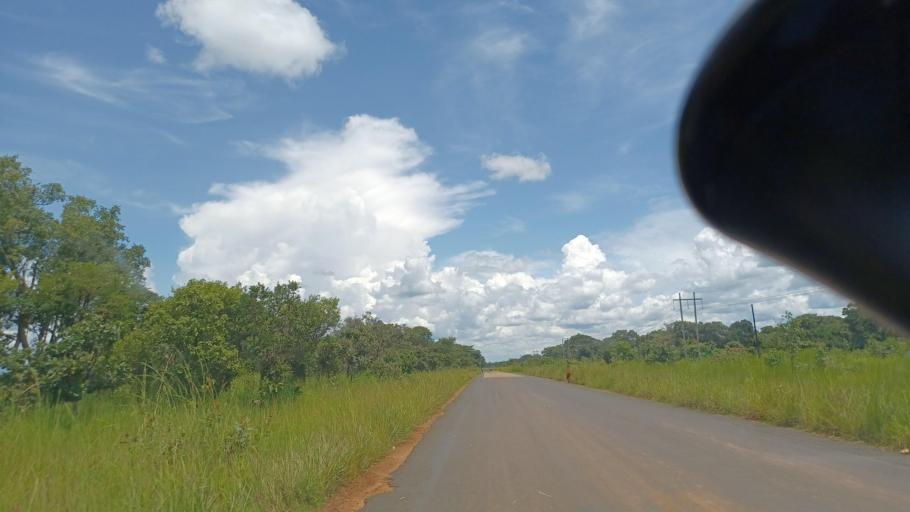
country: ZM
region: North-Western
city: Solwezi
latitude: -12.5672
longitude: 26.1378
